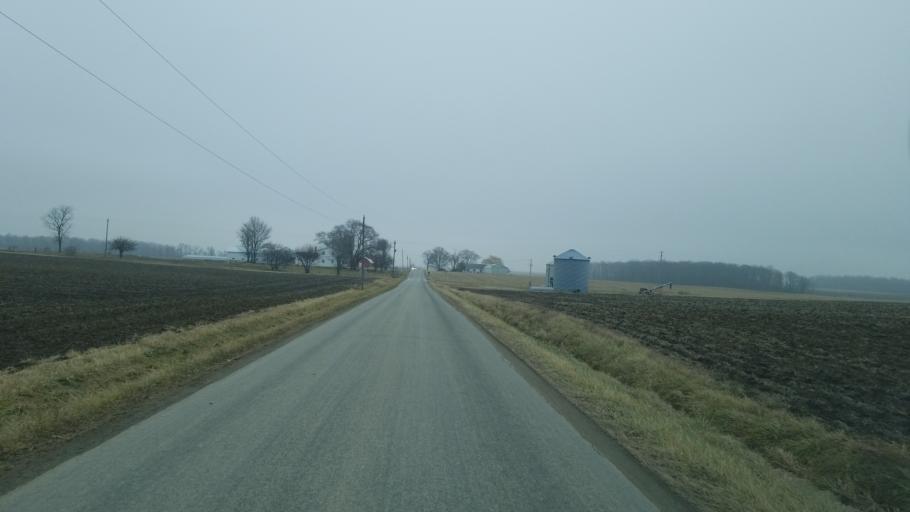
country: US
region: Indiana
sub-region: Adams County
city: Geneva
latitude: 40.5865
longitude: -84.8230
